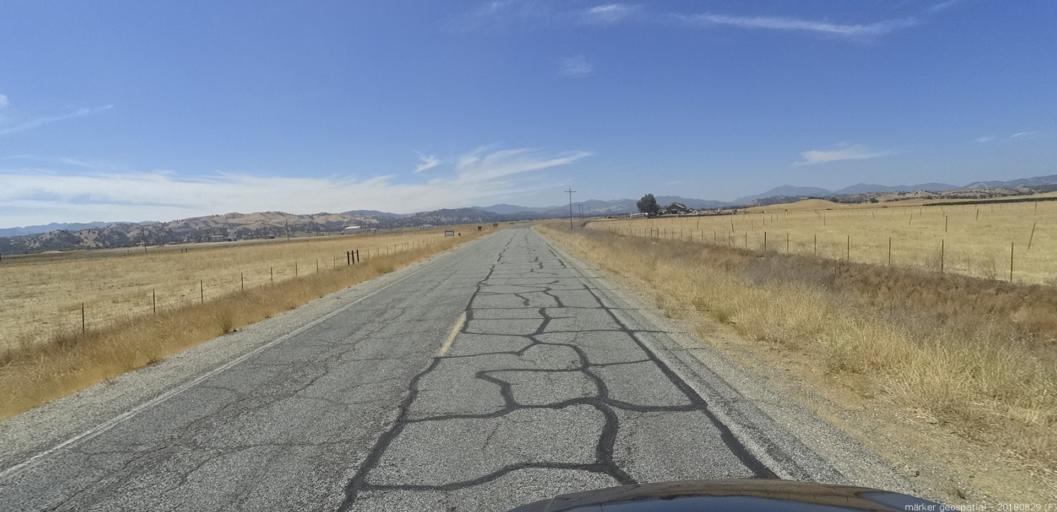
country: US
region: California
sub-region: Monterey County
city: King City
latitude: 35.9419
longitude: -121.1277
